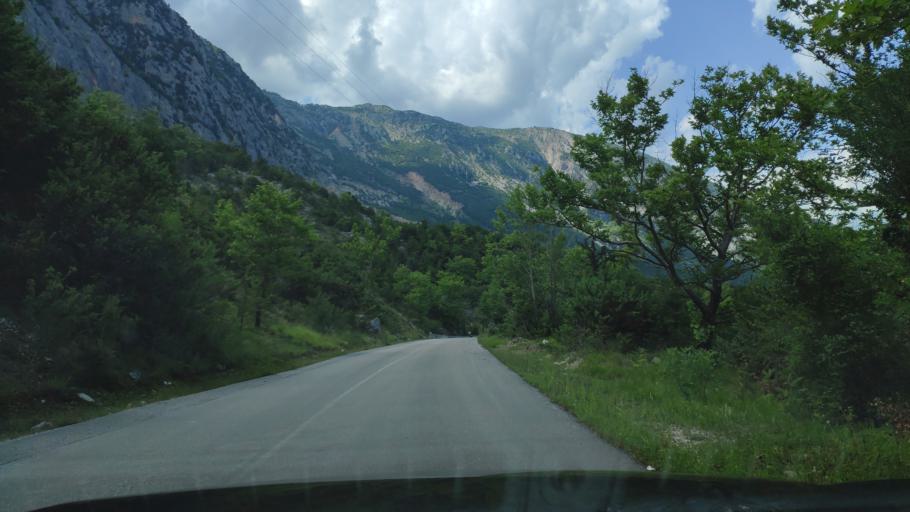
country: GR
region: Epirus
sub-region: Nomos Artas
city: Agios Dimitrios
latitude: 39.4290
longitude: 21.0162
